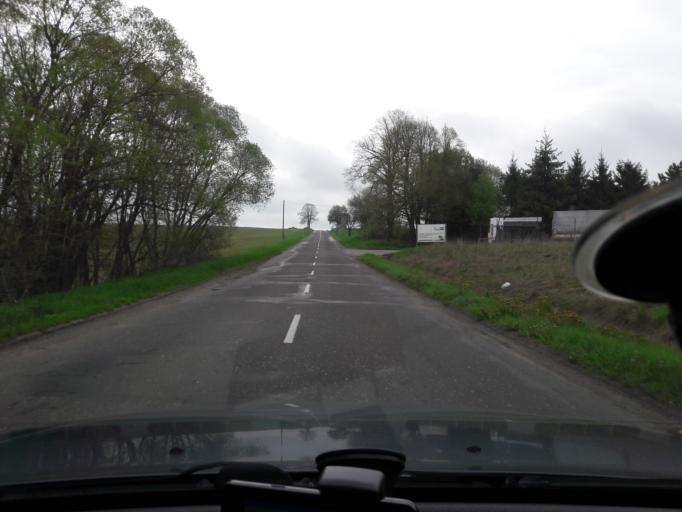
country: SK
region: Banskobystricky
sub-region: Okres Banska Bystrica
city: Brezno
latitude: 48.8001
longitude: 19.6774
